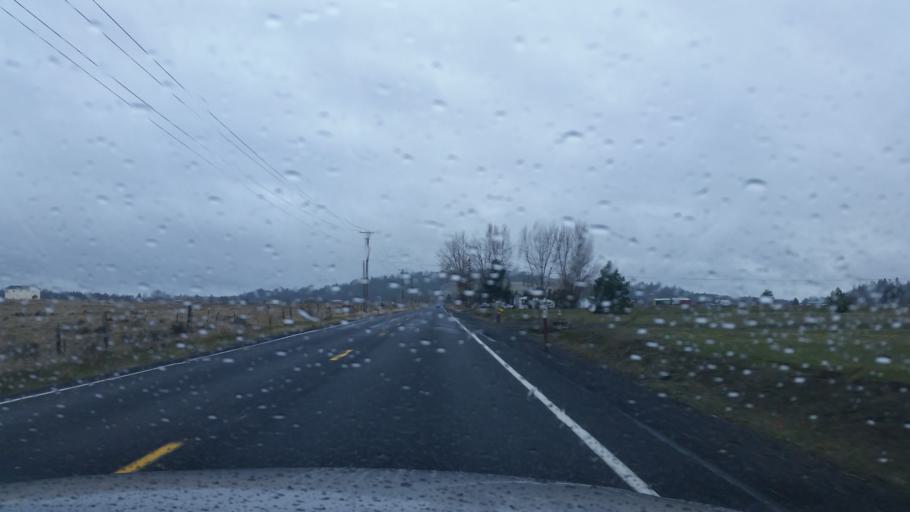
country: US
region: Washington
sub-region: Spokane County
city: Fairchild Air Force Base
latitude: 47.5758
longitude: -117.6076
